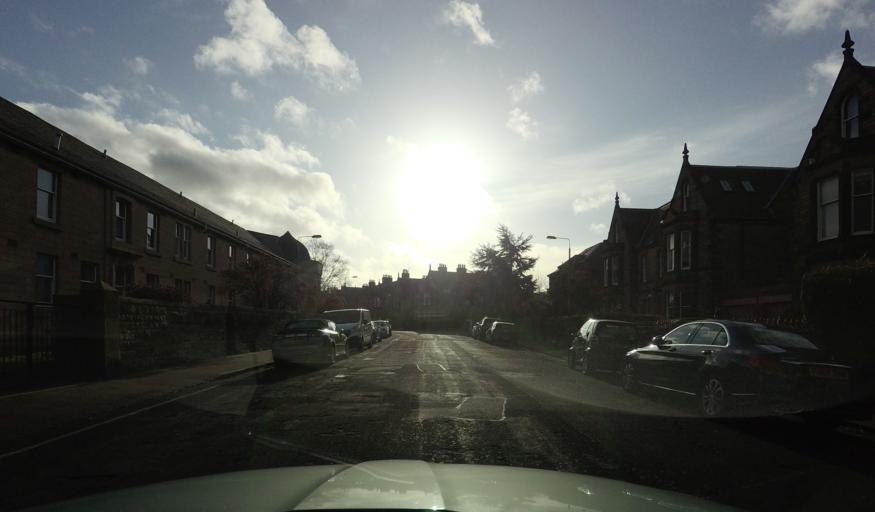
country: GB
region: Scotland
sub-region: Edinburgh
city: Edinburgh
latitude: 55.9783
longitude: -3.2097
